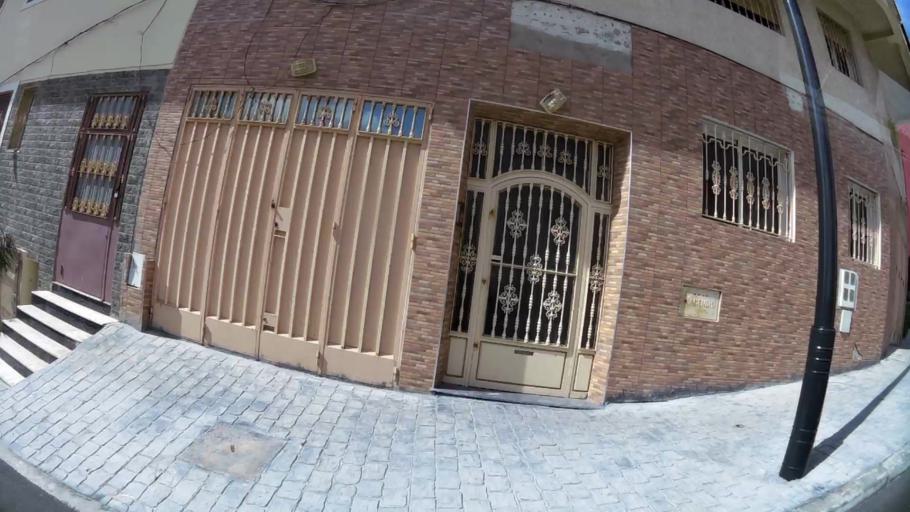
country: MA
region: Tanger-Tetouan
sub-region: Tanger-Assilah
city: Tangier
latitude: 35.7693
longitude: -5.7639
